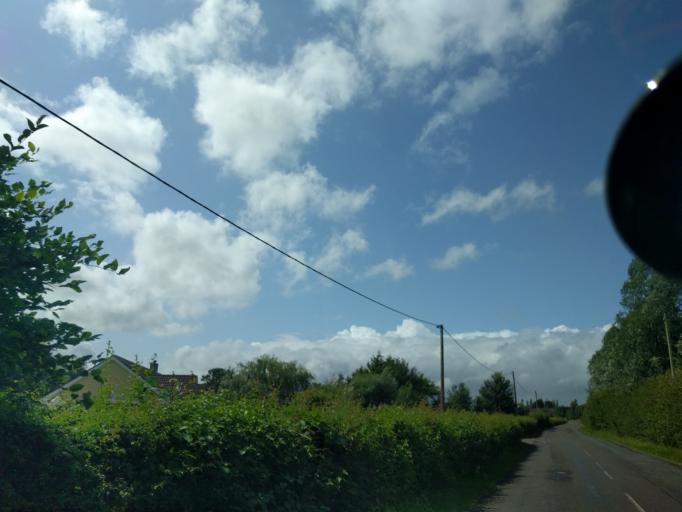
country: GB
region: England
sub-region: Wiltshire
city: Lyneham
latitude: 51.5303
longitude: -1.9945
